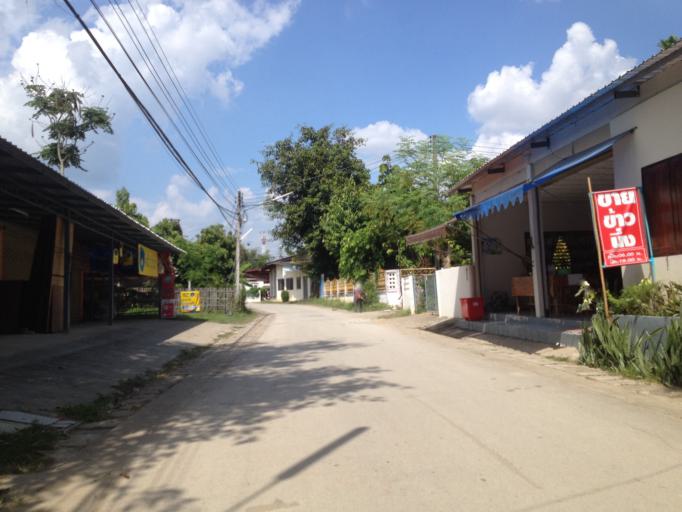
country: TH
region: Chiang Mai
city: Hang Dong
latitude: 18.7171
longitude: 98.9187
